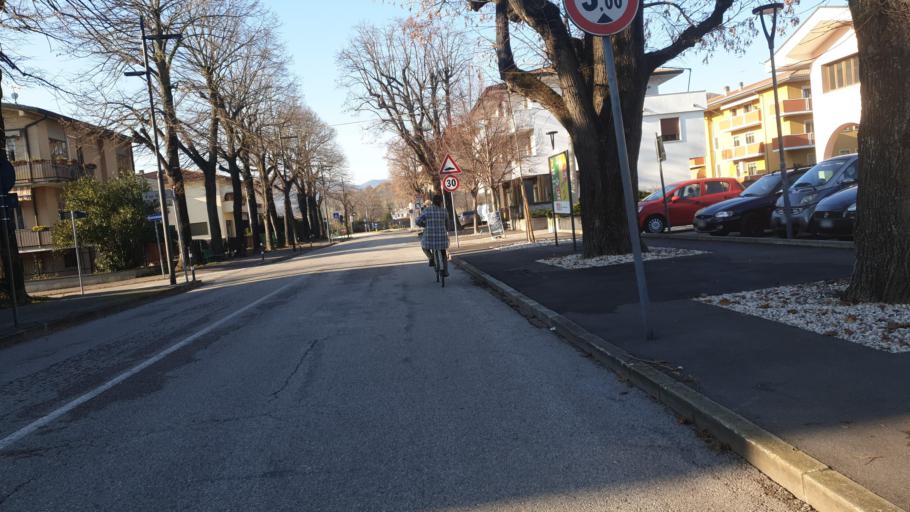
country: IT
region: Veneto
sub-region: Provincia di Padova
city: Battaglia Terme
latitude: 45.2893
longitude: 11.7797
